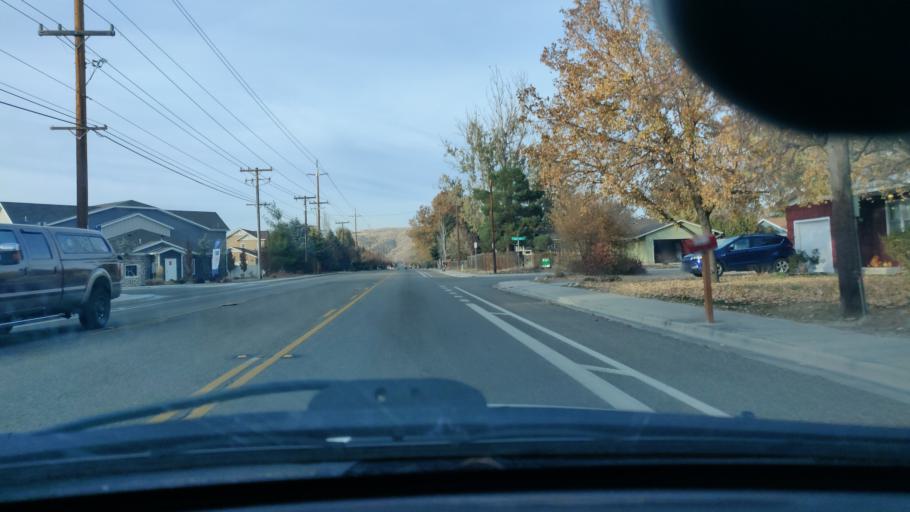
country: US
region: Idaho
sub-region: Ada County
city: Garden City
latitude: 43.6721
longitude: -116.2792
